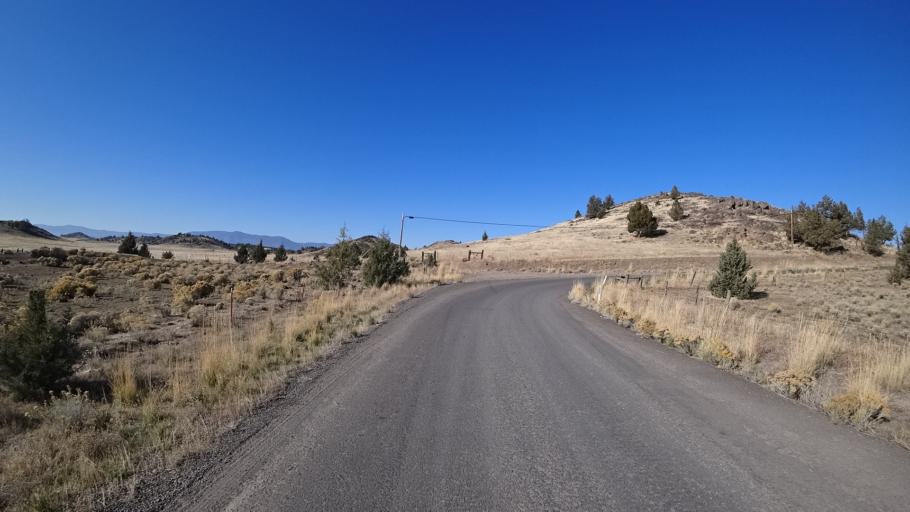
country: US
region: California
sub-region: Siskiyou County
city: Montague
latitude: 41.6965
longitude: -122.4372
